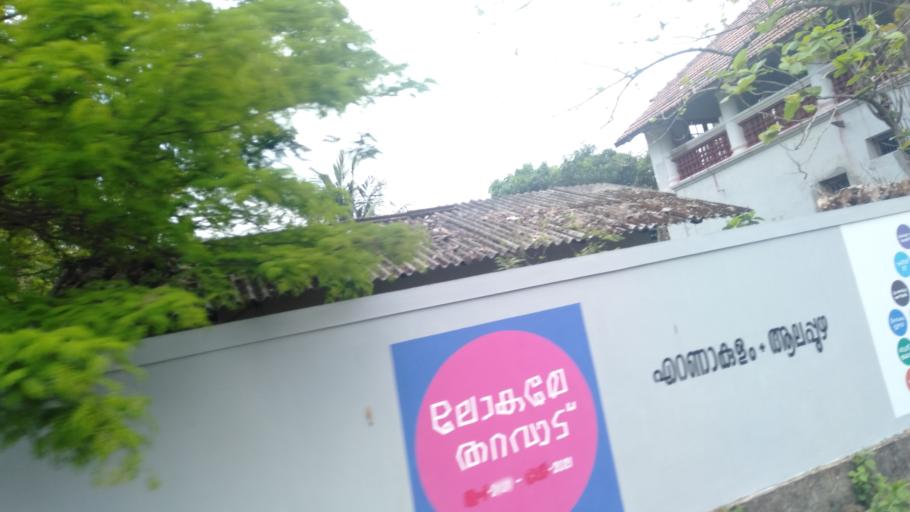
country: IN
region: Kerala
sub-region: Alappuzha
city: Alleppey
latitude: 9.4952
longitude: 76.3315
